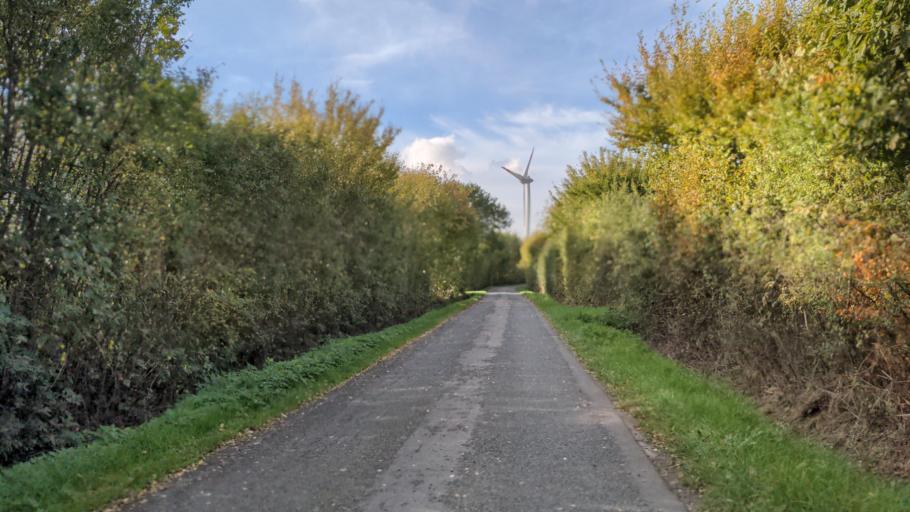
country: DE
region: Schleswig-Holstein
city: Monkhagen
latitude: 53.9305
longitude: 10.5740
